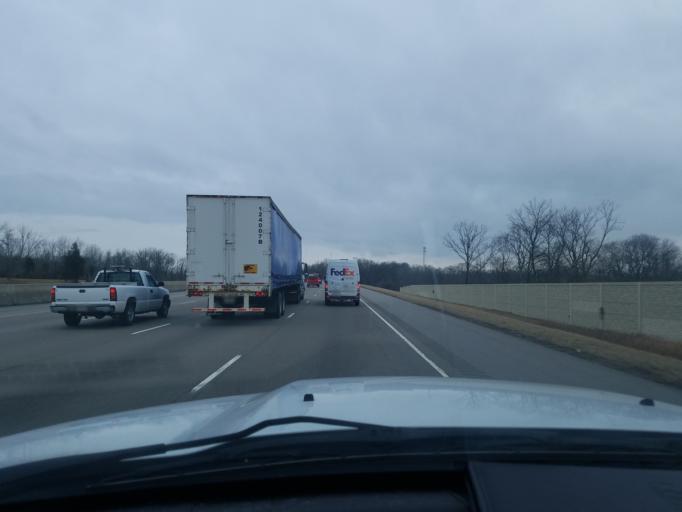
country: US
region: Ohio
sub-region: Warren County
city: Franklin
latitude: 39.5316
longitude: -84.3098
